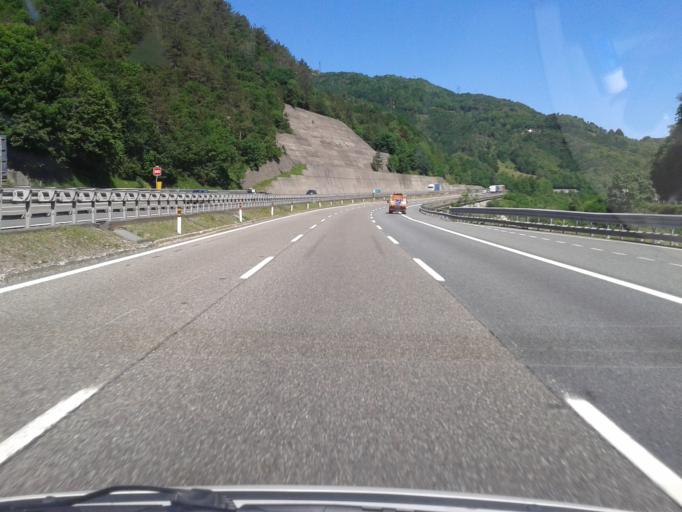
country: IT
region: Liguria
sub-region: Provincia di Genova
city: Masone
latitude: 44.5113
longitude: 8.7015
